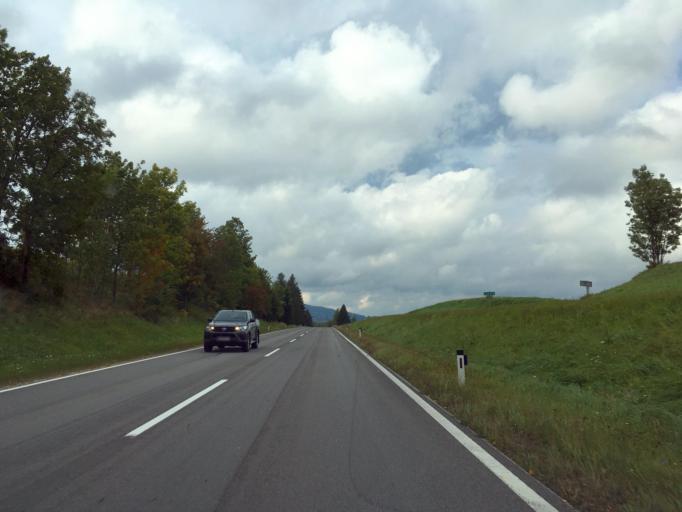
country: AT
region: Styria
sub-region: Politischer Bezirk Hartberg-Fuerstenfeld
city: Pinggau
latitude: 47.4624
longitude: 16.0617
